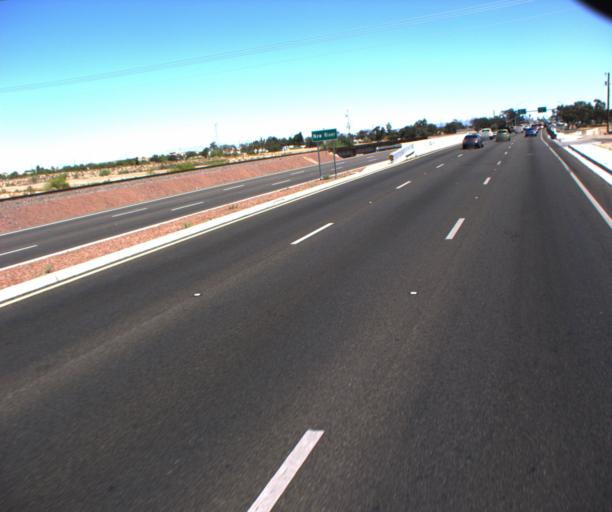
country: US
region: Arizona
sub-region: Maricopa County
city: Sun City
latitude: 33.5952
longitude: -112.2644
